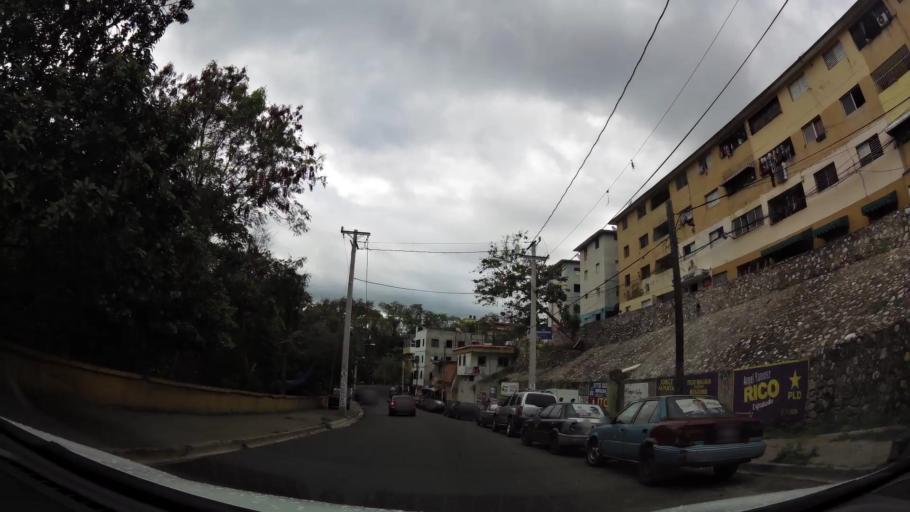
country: DO
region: Nacional
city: La Agustina
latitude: 18.4967
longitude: -69.9302
